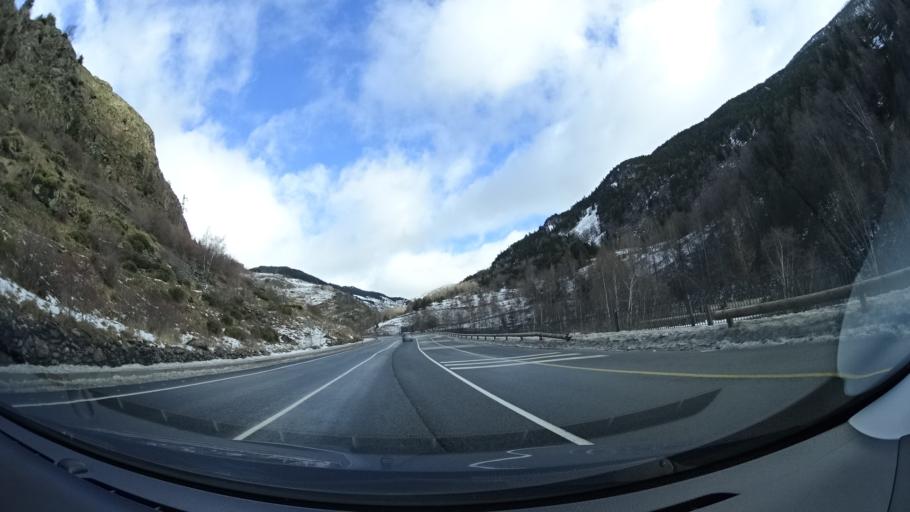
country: AD
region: Canillo
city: Canillo
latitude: 42.5757
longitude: 1.6230
